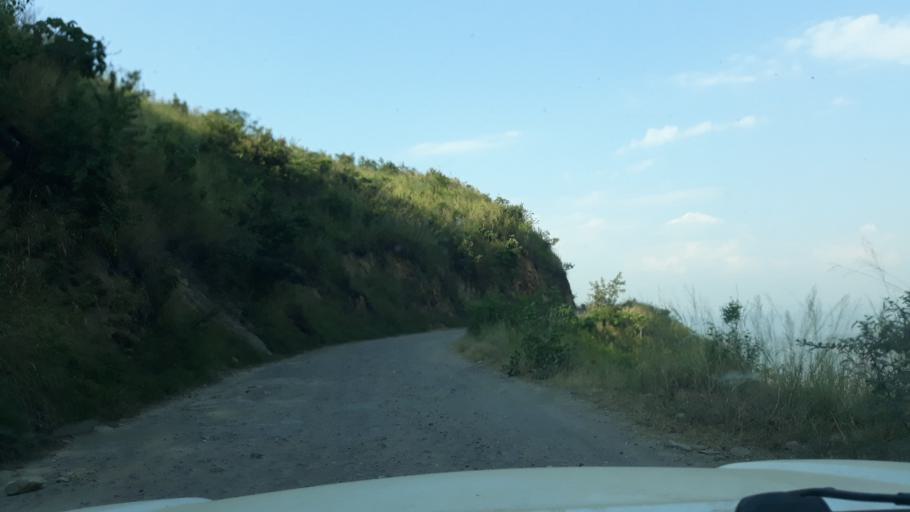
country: BI
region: Cibitoke
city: Cibitoke
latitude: -2.7065
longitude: 28.9900
